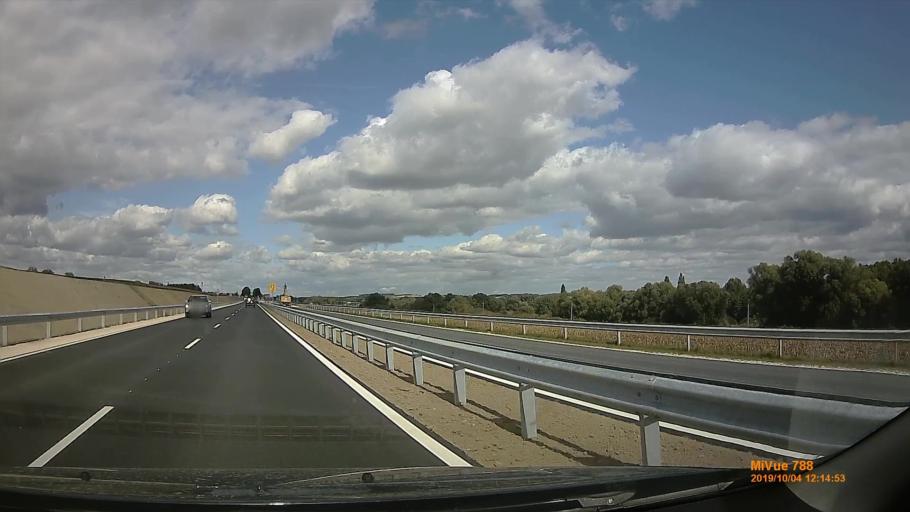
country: HU
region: Somogy
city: Karad
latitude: 46.5420
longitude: 17.8152
